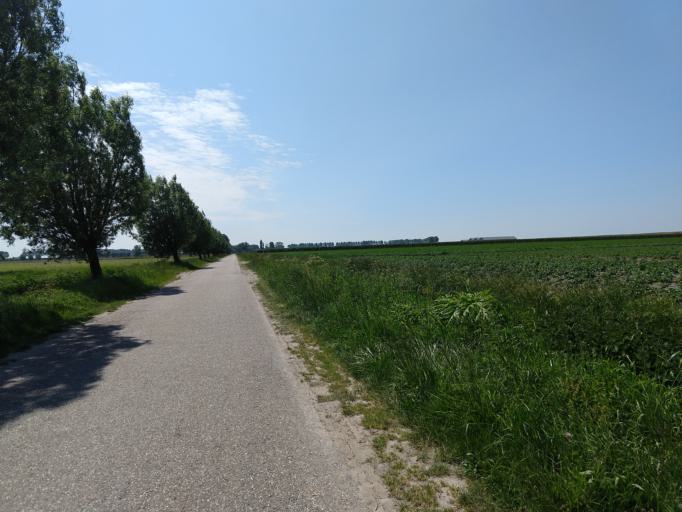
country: NL
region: Zeeland
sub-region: Schouwen-Duiveland
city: Bruinisse
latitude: 51.5996
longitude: 4.0413
